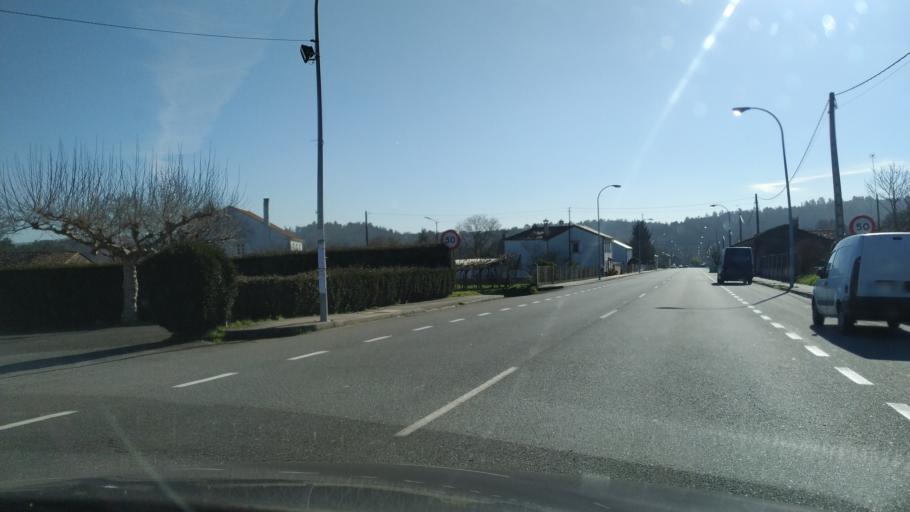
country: ES
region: Galicia
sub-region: Provincia de Pontevedra
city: Silleda
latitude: 42.7381
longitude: -8.3261
